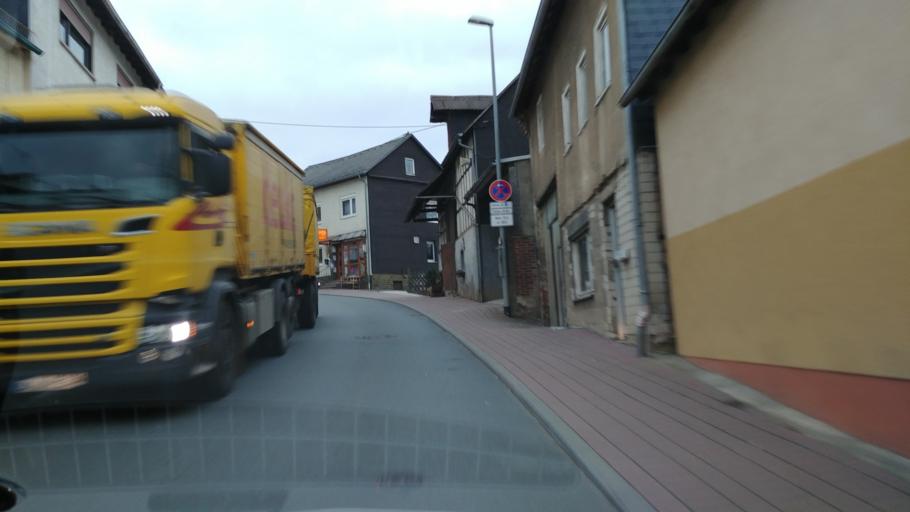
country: DE
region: Rheinland-Pfalz
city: Kaltenholzhausen
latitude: 50.2640
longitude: 8.1537
